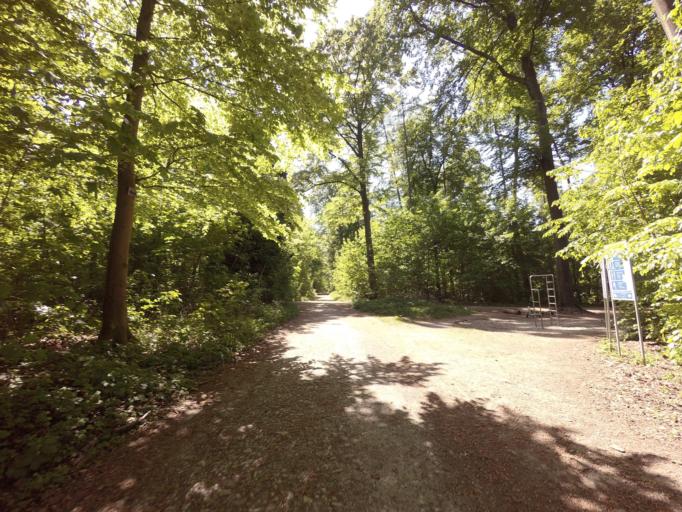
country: DE
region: Lower Saxony
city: Hildesheim
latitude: 52.1396
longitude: 9.9859
